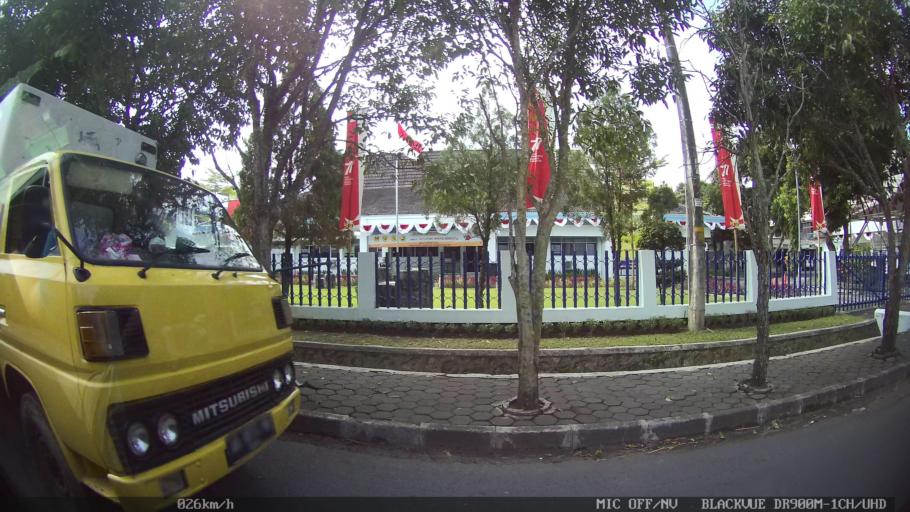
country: ID
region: Daerah Istimewa Yogyakarta
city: Depok
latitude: -7.7607
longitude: 110.4294
